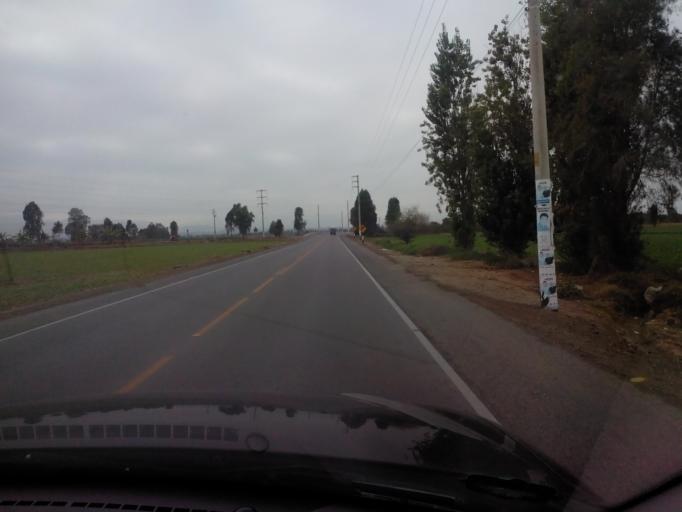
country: PE
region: Ica
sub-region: Provincia de Pisco
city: Independencia
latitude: -13.6831
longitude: -76.0575
